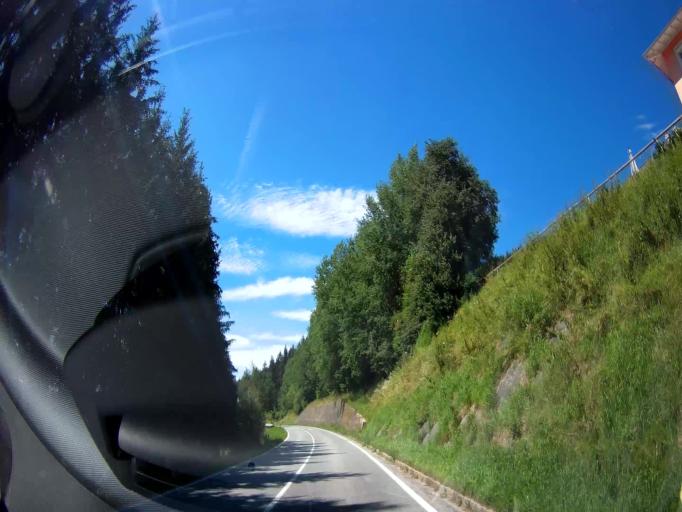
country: AT
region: Carinthia
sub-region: Politischer Bezirk Sankt Veit an der Glan
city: Glodnitz
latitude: 46.8513
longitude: 14.1873
